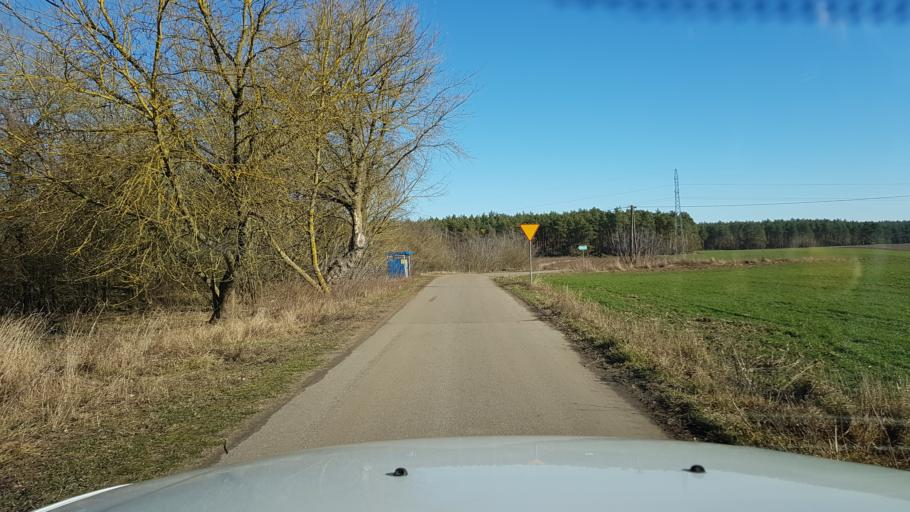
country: PL
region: West Pomeranian Voivodeship
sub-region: Powiat pyrzycki
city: Przelewice
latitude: 53.0497
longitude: 15.0580
